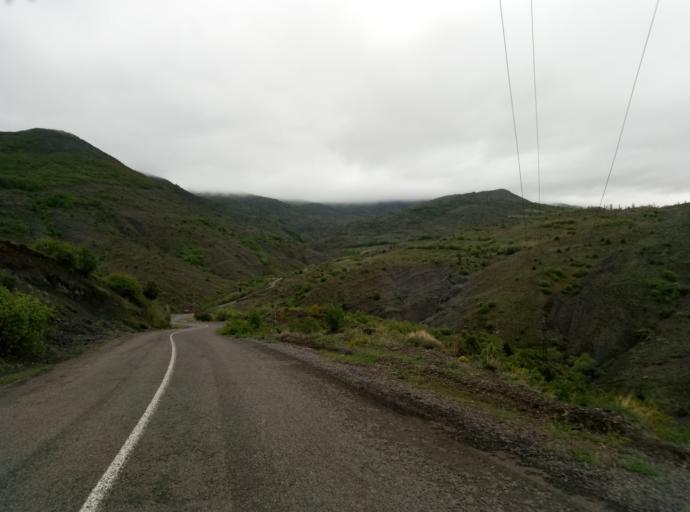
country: TR
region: Sivas
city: Koyulhisar
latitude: 40.1730
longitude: 37.9023
